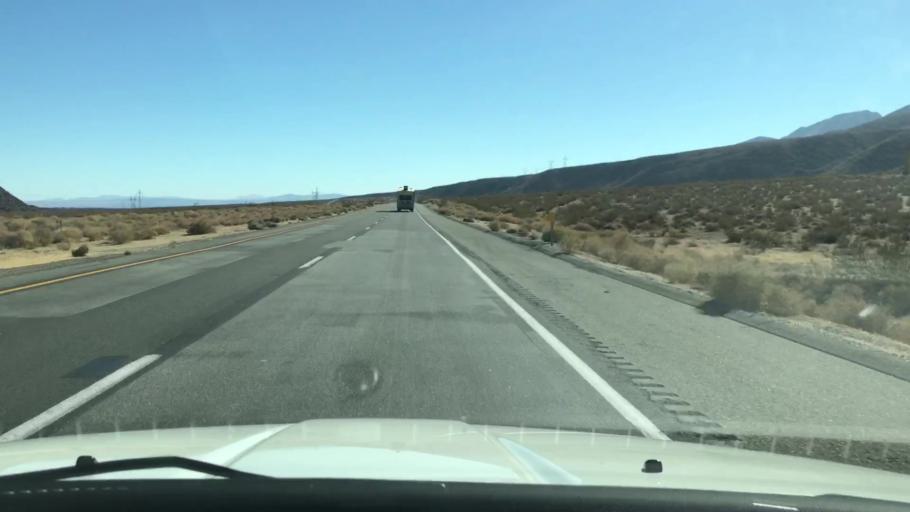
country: US
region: California
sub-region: Kern County
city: Inyokern
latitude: 35.9010
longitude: -117.9000
